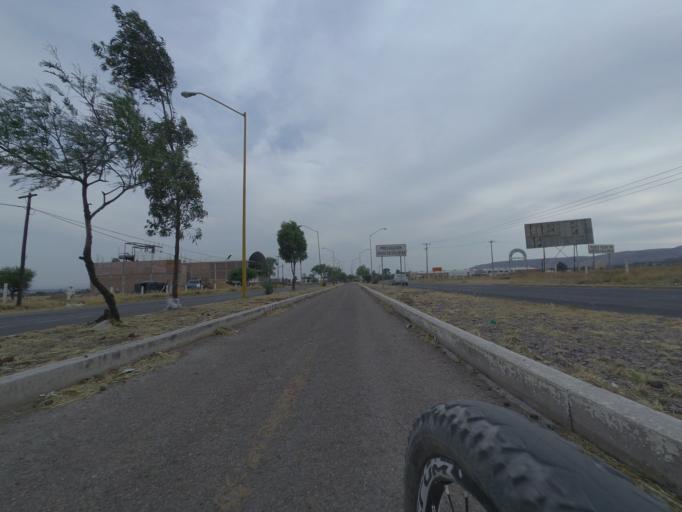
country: MX
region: Aguascalientes
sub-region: Aguascalientes
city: La Loma de los Negritos
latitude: 21.8696
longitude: -102.3709
